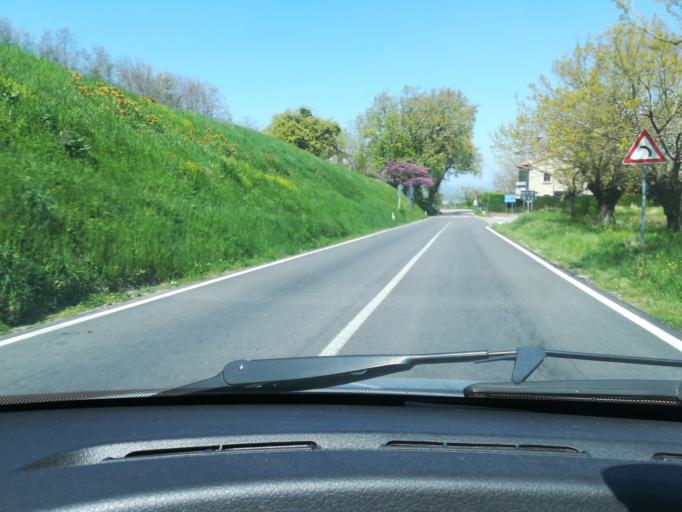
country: IT
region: The Marches
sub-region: Provincia di Macerata
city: Cingoli
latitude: 43.3780
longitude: 13.2164
